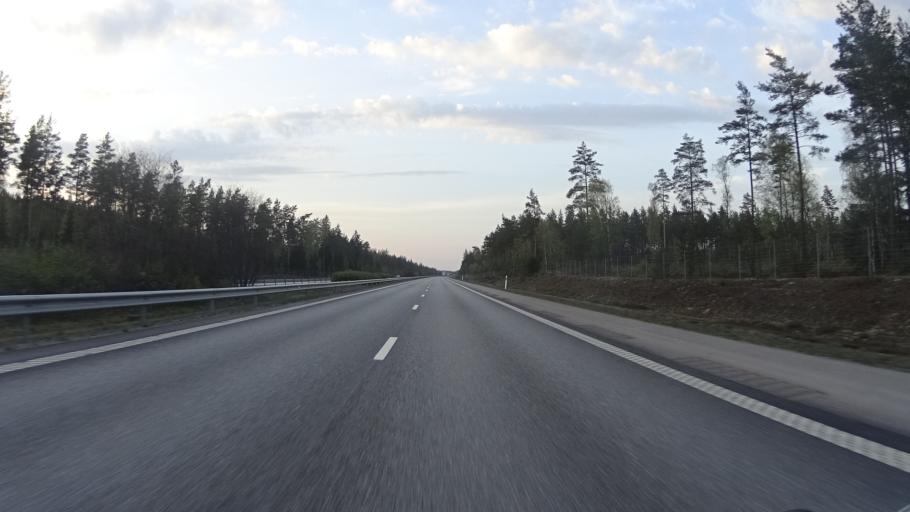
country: SE
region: Joenkoeping
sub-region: Vaggeryds Kommun
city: Skillingaryd
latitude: 57.3949
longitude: 14.0999
